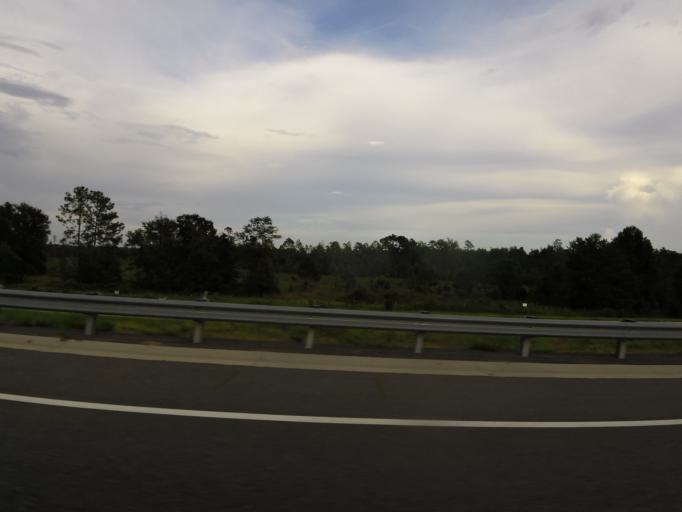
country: US
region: Florida
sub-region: Clay County
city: Lakeside
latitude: 30.1294
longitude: -81.8304
